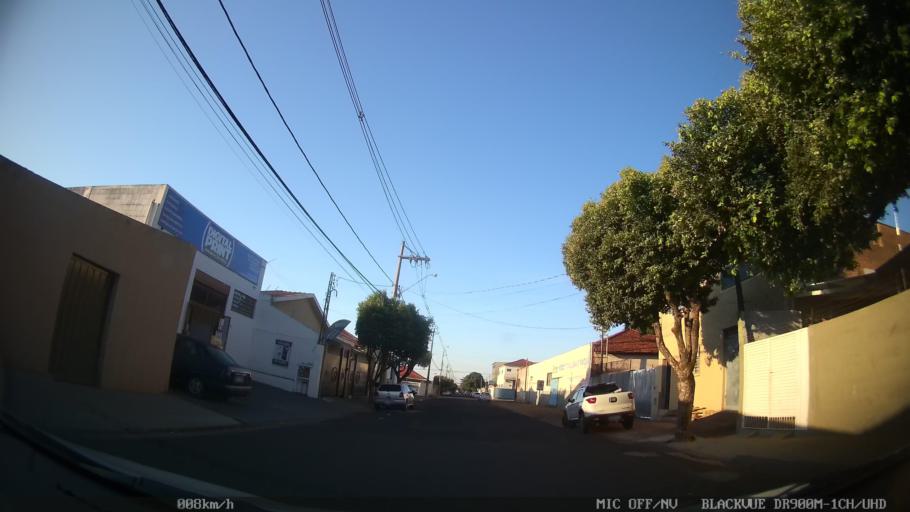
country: BR
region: Sao Paulo
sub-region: Sao Jose Do Rio Preto
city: Sao Jose do Rio Preto
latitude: -20.7964
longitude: -49.3892
